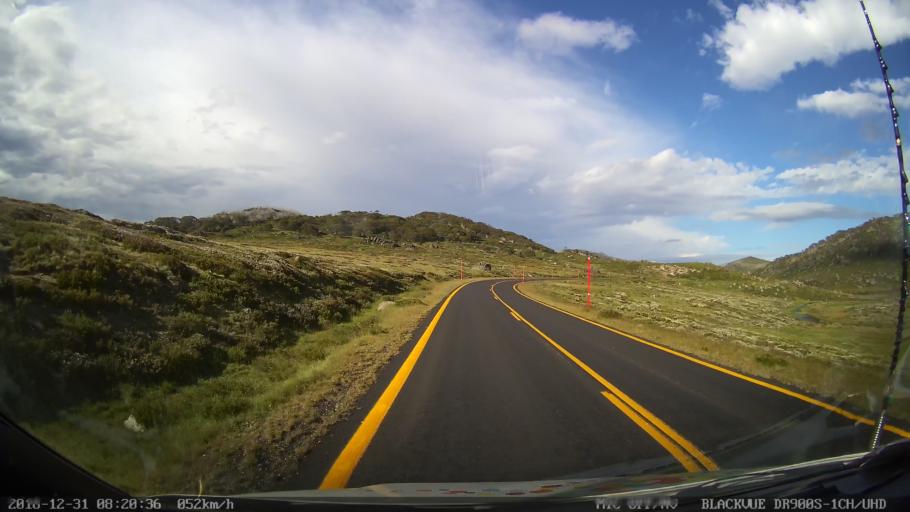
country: AU
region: New South Wales
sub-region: Snowy River
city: Jindabyne
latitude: -36.4256
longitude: 148.3749
